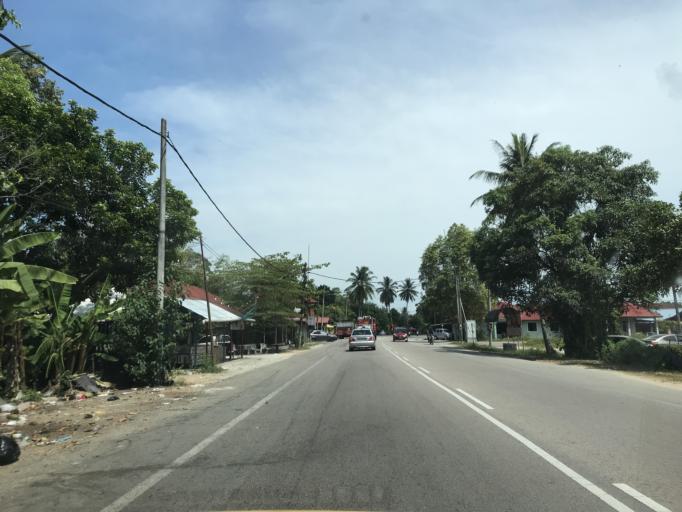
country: MY
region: Kelantan
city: Kota Bharu
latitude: 6.1201
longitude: 102.1890
